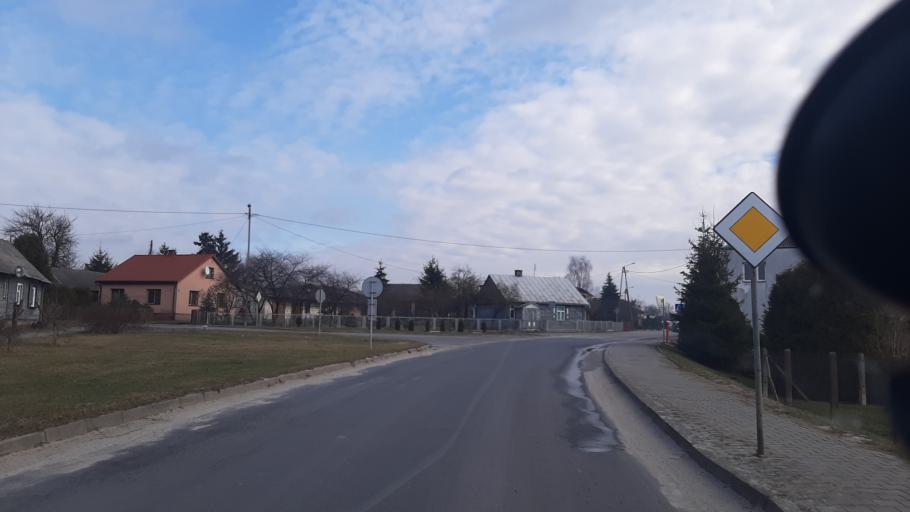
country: PL
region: Lublin Voivodeship
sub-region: Powiat lubartowski
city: Ostrow Lubelski
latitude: 51.4941
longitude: 22.8563
